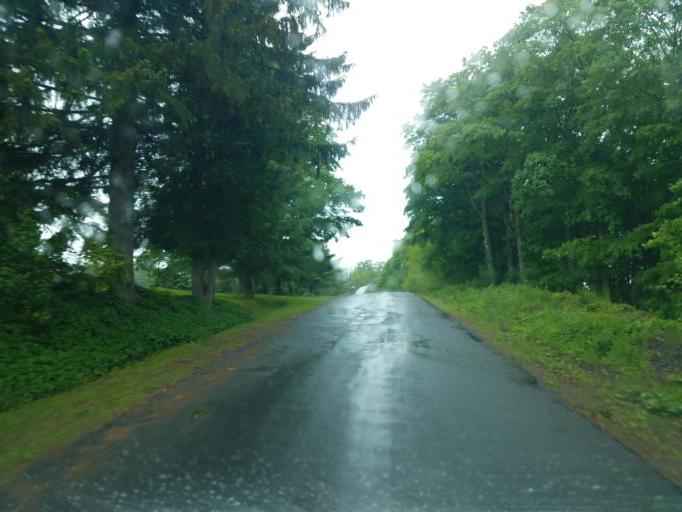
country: US
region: New York
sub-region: Herkimer County
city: Ilion
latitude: 42.9544
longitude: -75.0285
